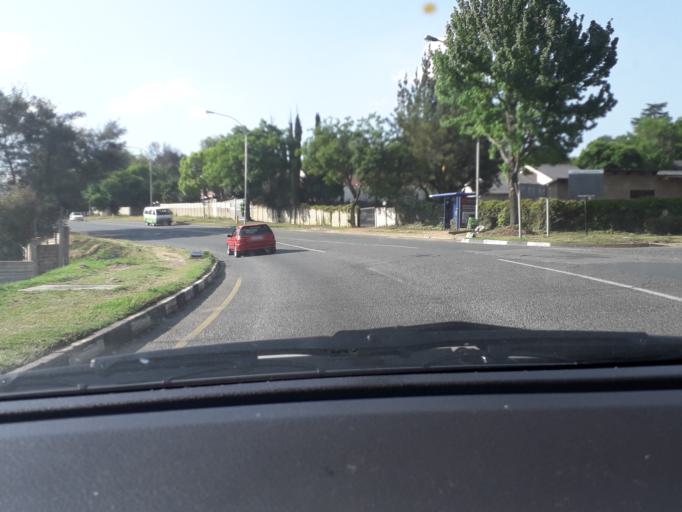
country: ZA
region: Gauteng
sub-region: City of Johannesburg Metropolitan Municipality
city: Modderfontein
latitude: -26.1267
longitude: 28.1243
